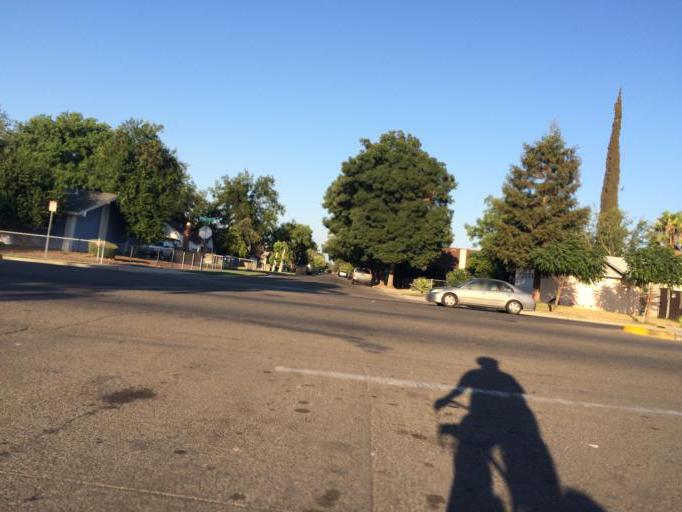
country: US
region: California
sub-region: Fresno County
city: Fresno
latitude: 36.7478
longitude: -119.7367
